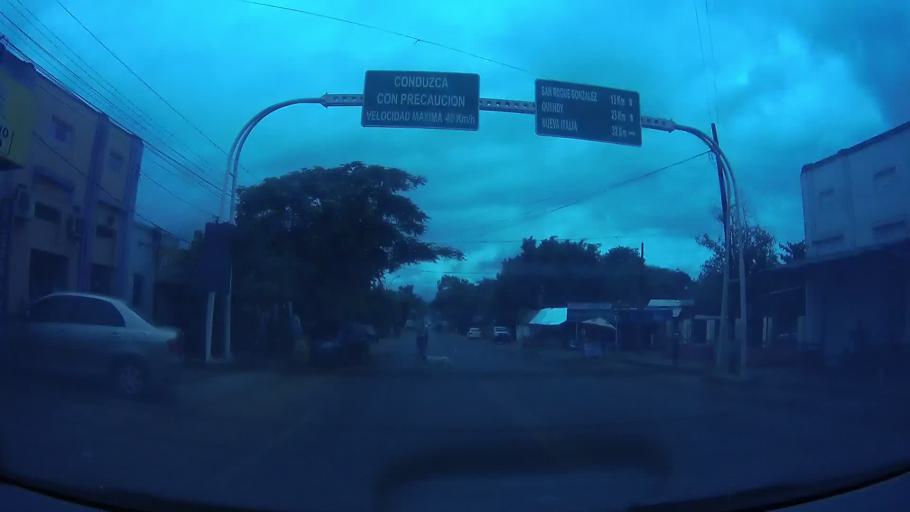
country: PY
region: Paraguari
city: Carapegua
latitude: -25.7697
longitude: -57.2443
